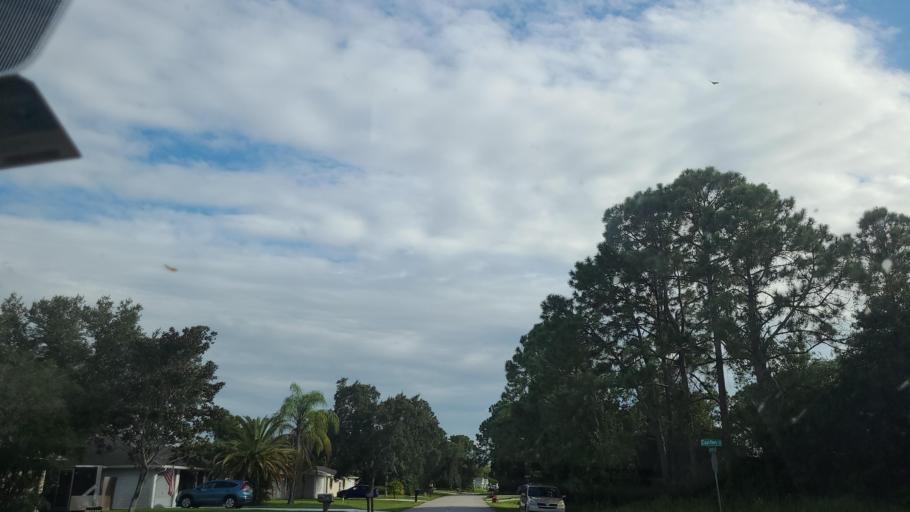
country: US
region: Florida
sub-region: Brevard County
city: Palm Bay
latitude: 27.9736
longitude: -80.6622
